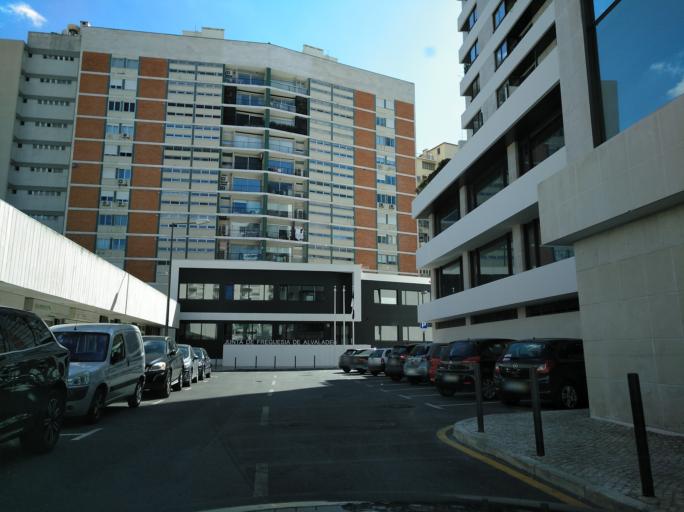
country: PT
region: Lisbon
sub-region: Lisbon
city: Lisbon
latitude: 38.7469
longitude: -9.1394
